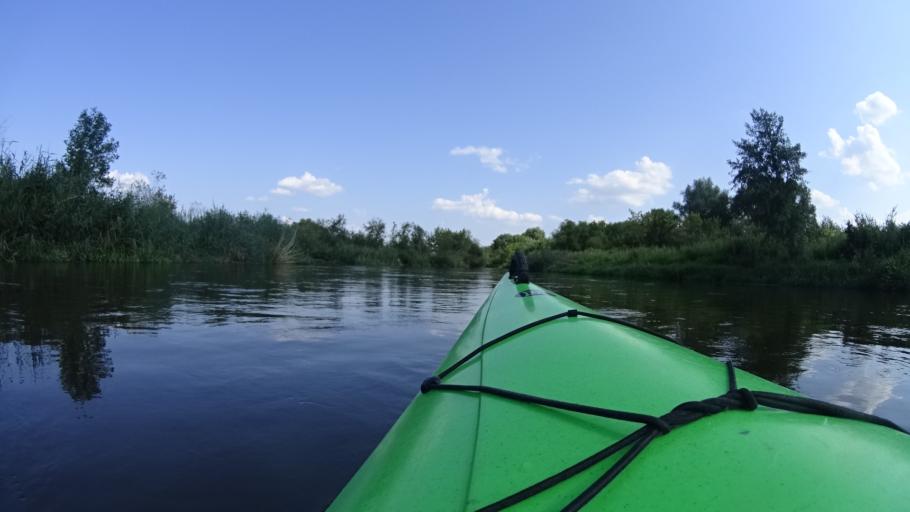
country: PL
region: Masovian Voivodeship
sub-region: Powiat bialobrzeski
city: Bialobrzegi
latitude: 51.6641
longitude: 20.8961
